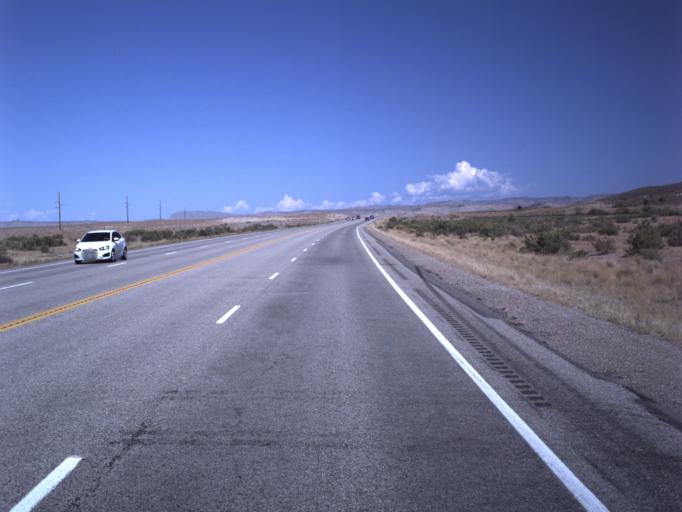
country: US
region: Utah
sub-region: Grand County
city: Moab
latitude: 38.8495
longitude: -109.8001
